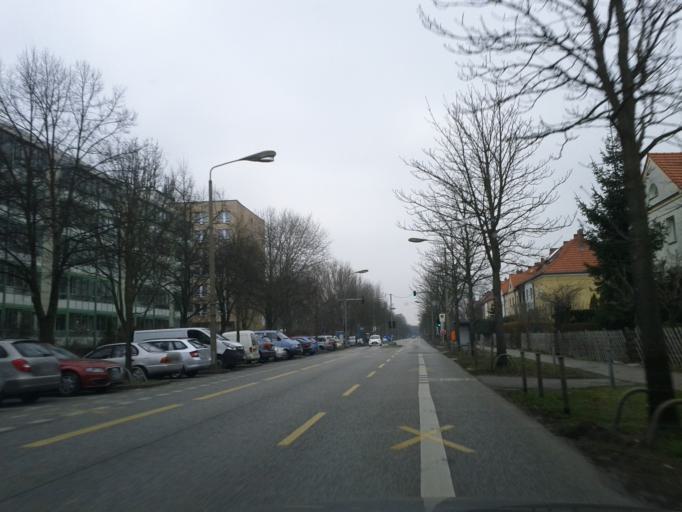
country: DE
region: Berlin
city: Johannisthal
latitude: 52.4534
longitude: 13.5071
